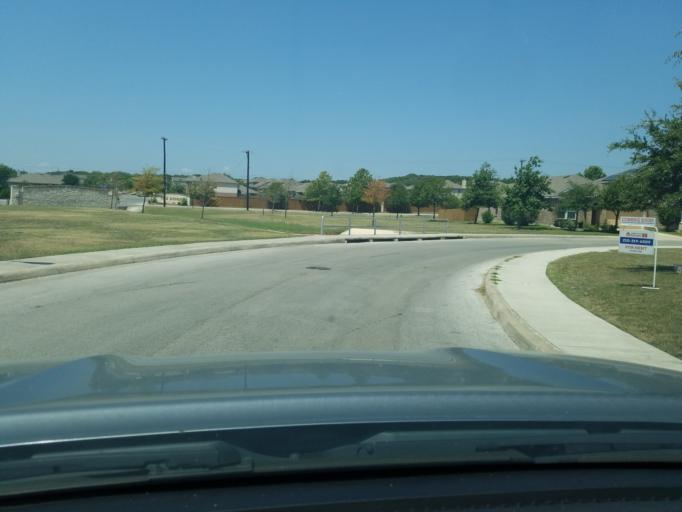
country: US
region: Texas
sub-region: Bexar County
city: Timberwood Park
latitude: 29.7029
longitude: -98.4807
